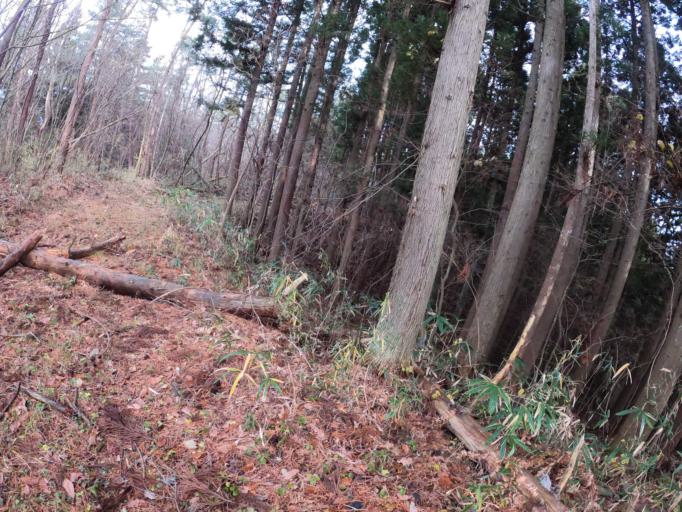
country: JP
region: Iwate
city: Ichinoseki
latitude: 38.8817
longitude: 141.1301
